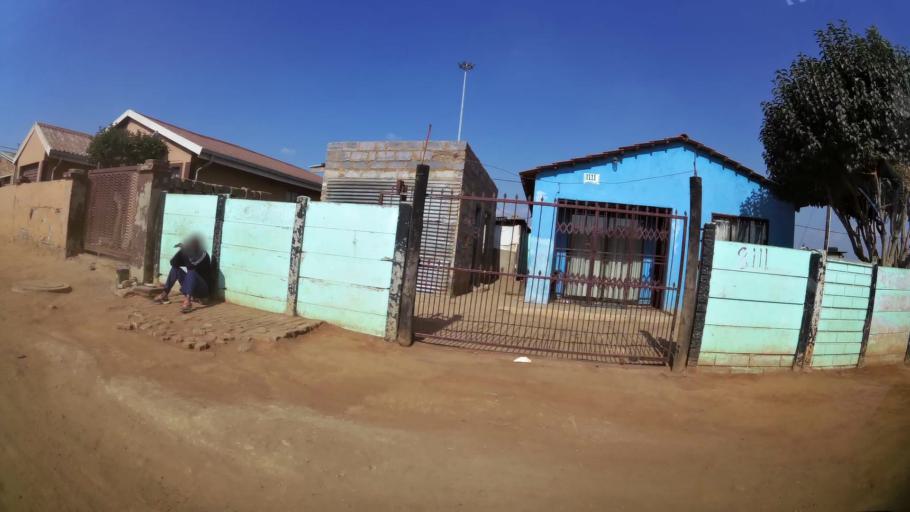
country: ZA
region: Gauteng
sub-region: Ekurhuleni Metropolitan Municipality
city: Springs
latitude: -26.1145
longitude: 28.4795
